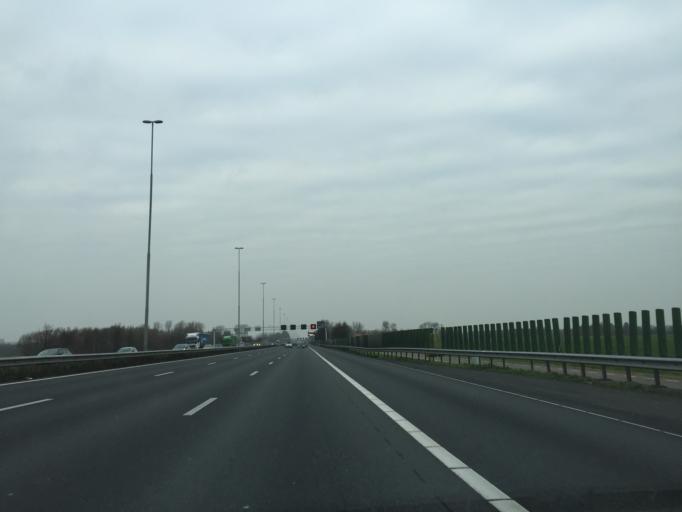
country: NL
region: South Holland
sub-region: Gemeente Schiedam
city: Schiedam
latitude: 51.9727
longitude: 4.3993
